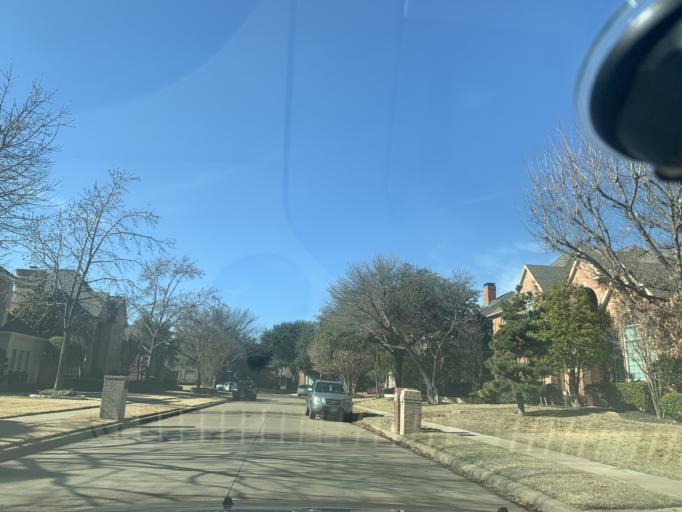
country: US
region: Texas
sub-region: Denton County
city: The Colony
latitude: 33.0512
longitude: -96.8150
